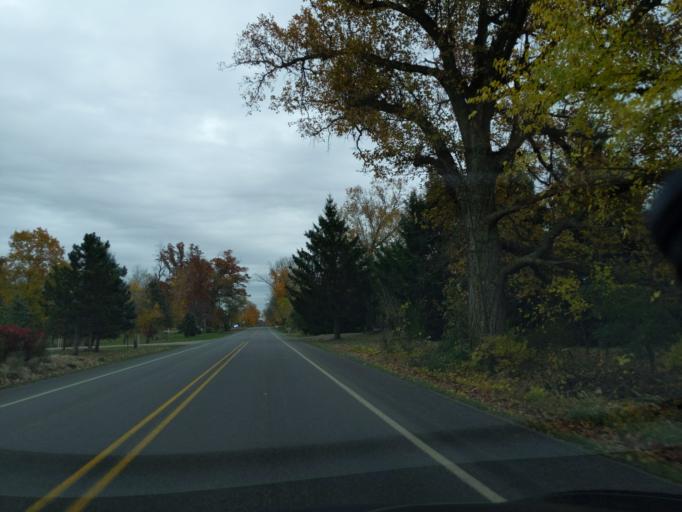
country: US
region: Michigan
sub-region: Jackson County
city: Spring Arbor
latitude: 42.2767
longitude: -84.5431
